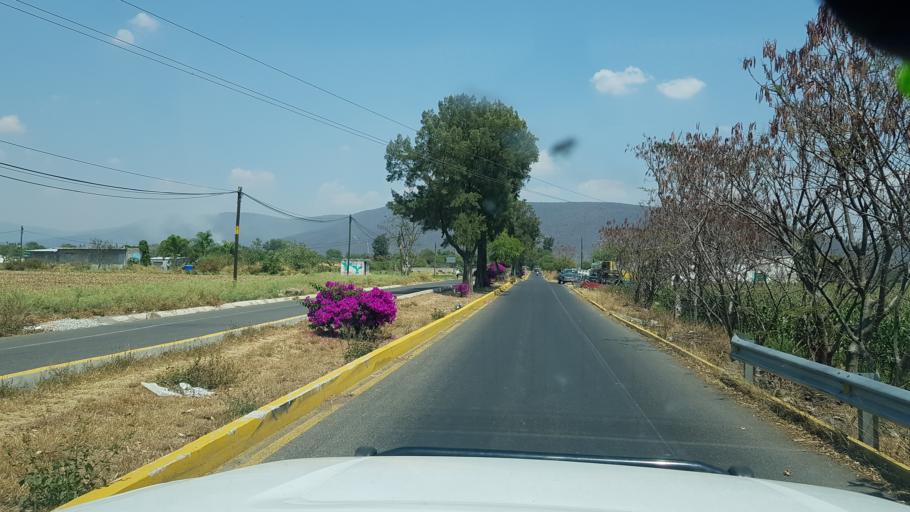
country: MX
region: Puebla
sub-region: Huaquechula
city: Cacaloxuchitl
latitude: 18.7901
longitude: -98.4604
